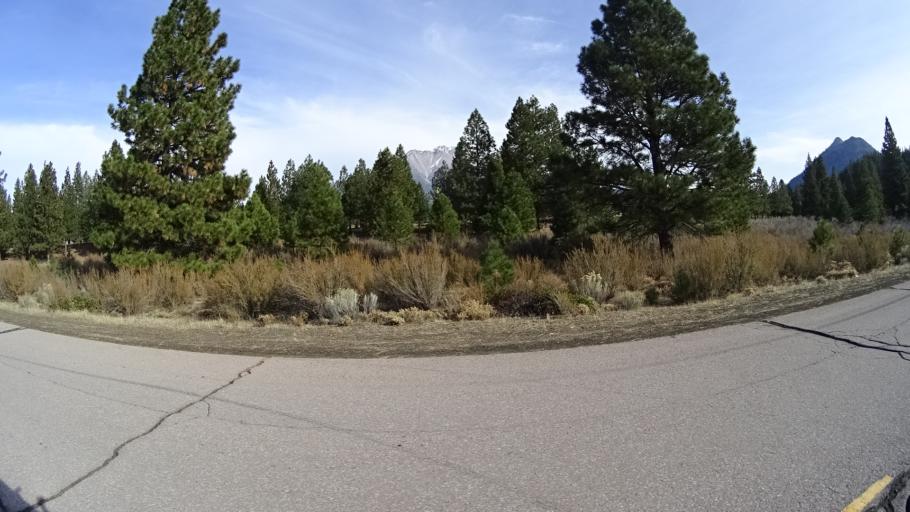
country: US
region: California
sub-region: Siskiyou County
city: Weed
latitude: 41.3971
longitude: -122.3830
